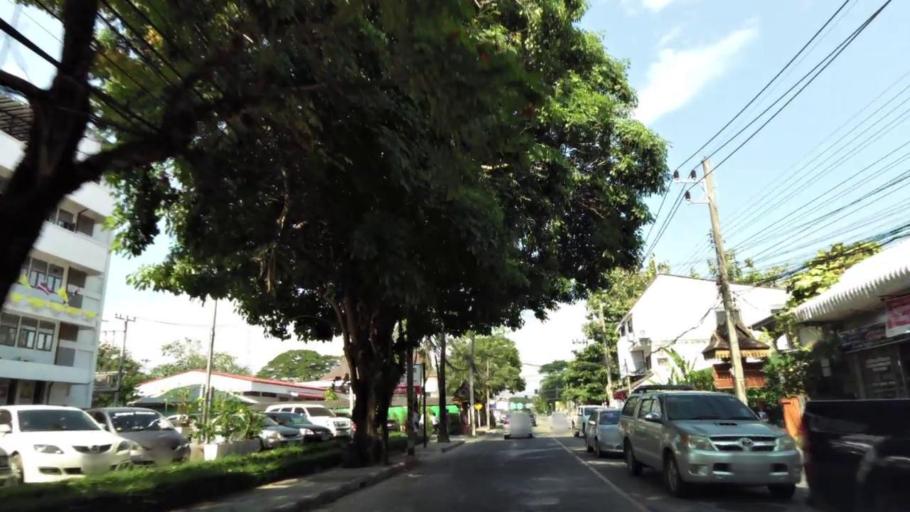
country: TH
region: Chiang Rai
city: Chiang Rai
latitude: 19.9113
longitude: 99.8327
